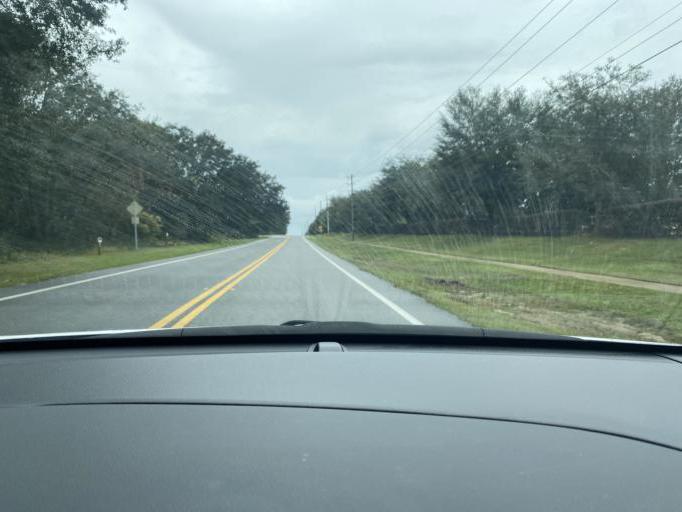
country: US
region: Florida
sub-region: Lake County
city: Groveland
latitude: 28.5769
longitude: -81.8607
